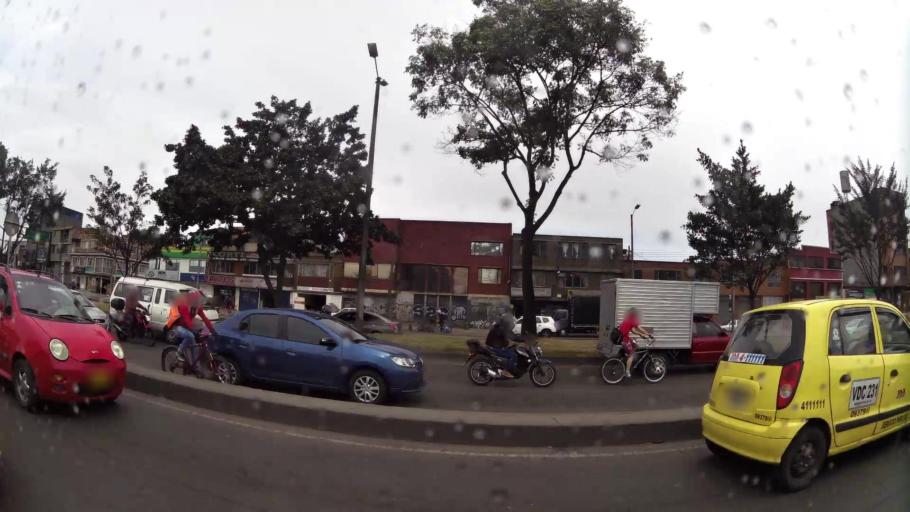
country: CO
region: Bogota D.C.
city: Bogota
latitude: 4.6358
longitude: -74.1197
